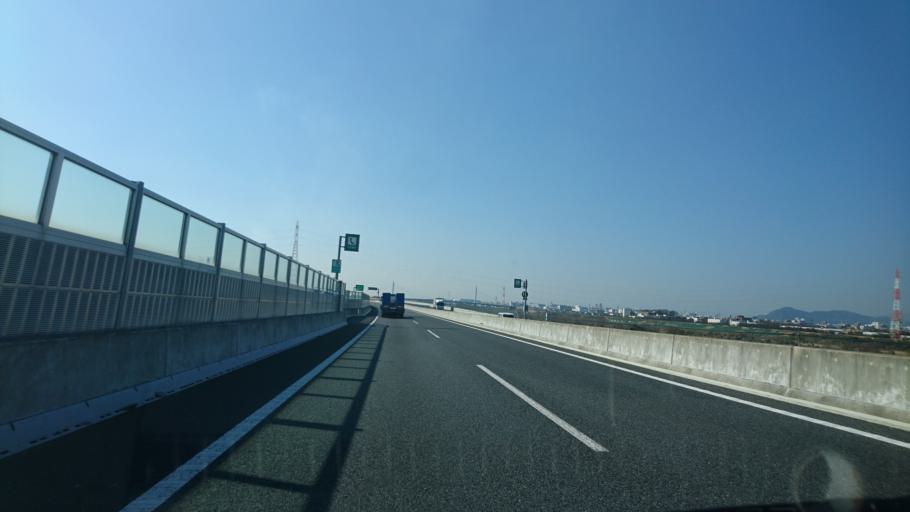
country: JP
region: Kanagawa
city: Chigasaki
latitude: 35.3682
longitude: 139.3734
